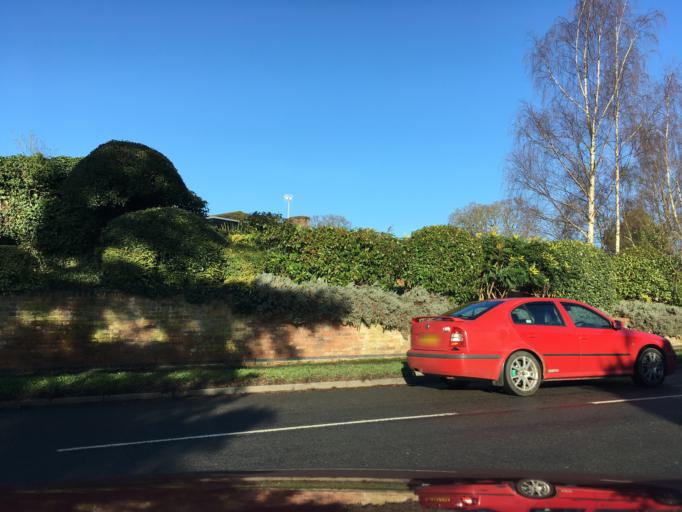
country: GB
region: England
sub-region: Warwickshire
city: Warwick
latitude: 52.2486
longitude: -1.5969
